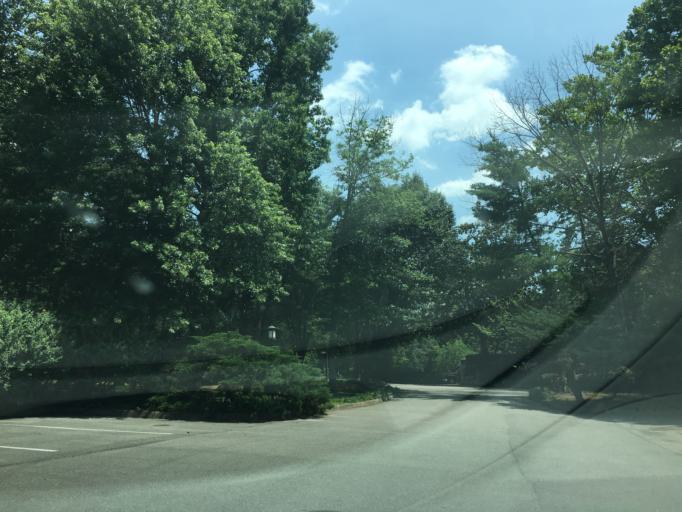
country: US
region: Tennessee
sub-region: Davidson County
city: Belle Meade
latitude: 36.0756
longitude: -86.9161
